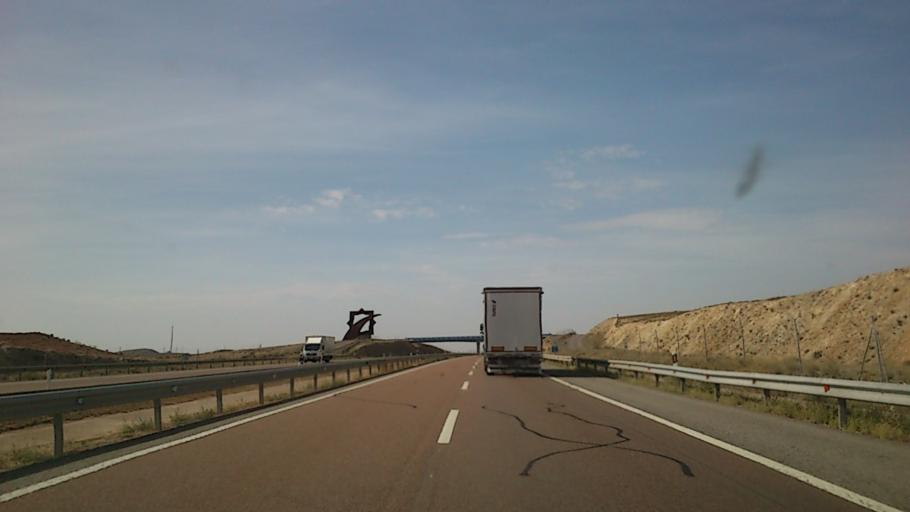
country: ES
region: Aragon
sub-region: Provincia de Teruel
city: Singra
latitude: 40.6374
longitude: -1.3119
